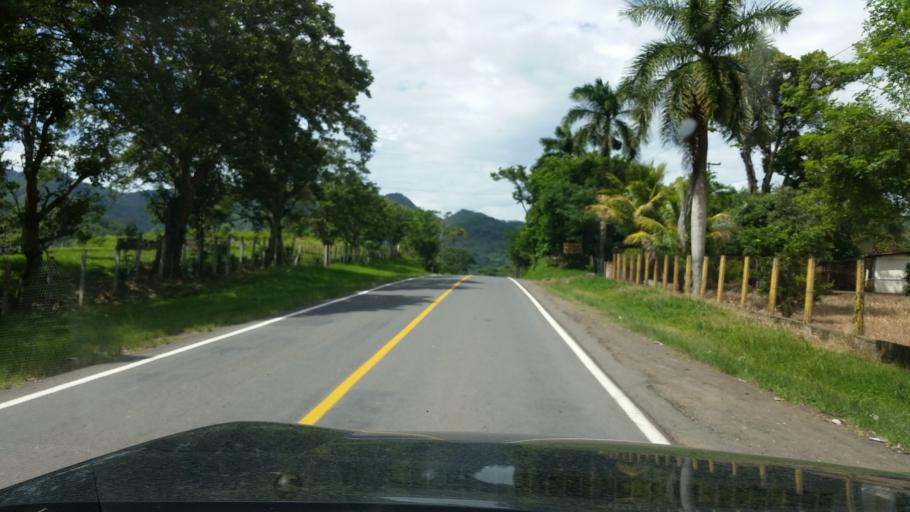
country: NI
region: Matagalpa
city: San Ramon
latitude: 12.9437
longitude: -85.8757
